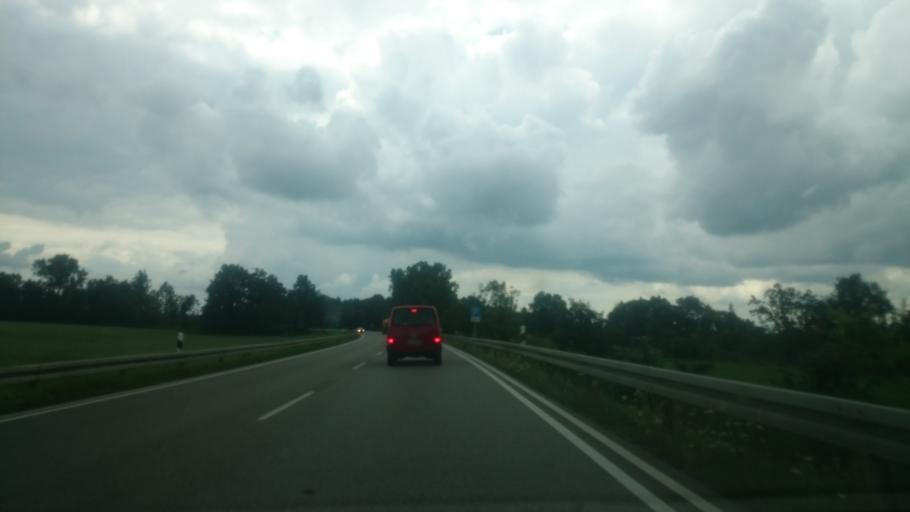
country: DE
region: Bavaria
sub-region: Swabia
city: Mauerstetten
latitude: 47.8817
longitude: 10.6448
